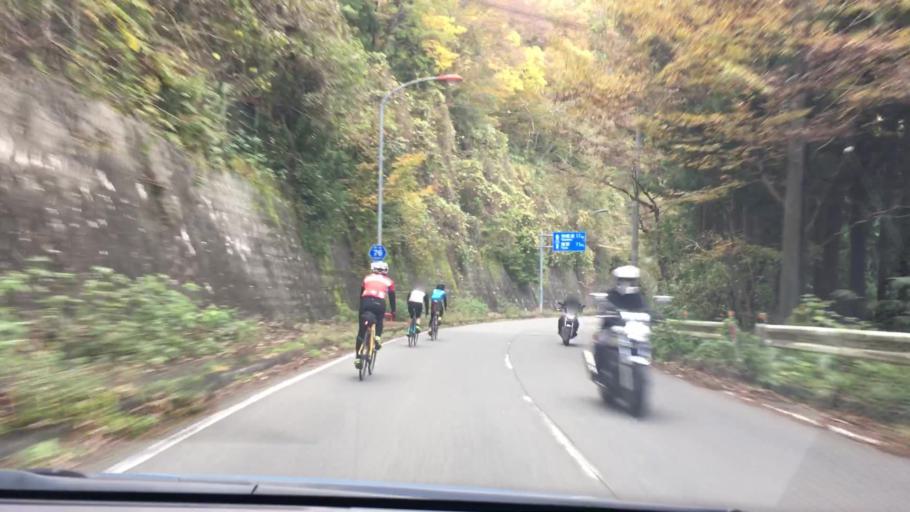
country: JP
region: Yamanashi
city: Uenohara
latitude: 35.5472
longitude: 139.1337
